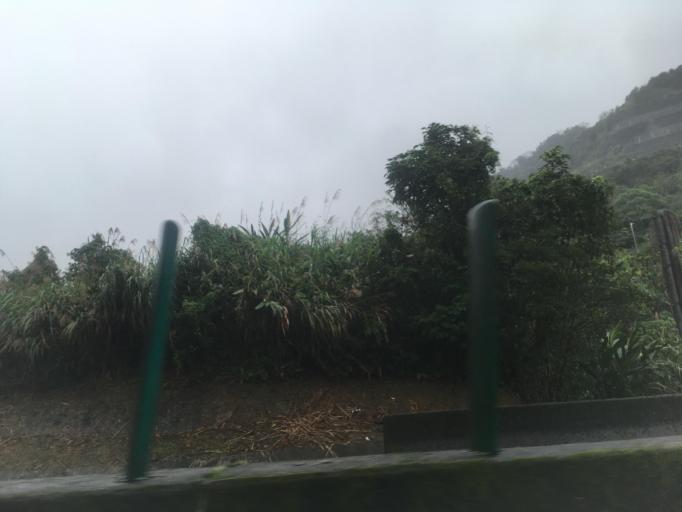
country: TW
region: Taiwan
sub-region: Keelung
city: Keelung
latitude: 25.1127
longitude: 121.6897
